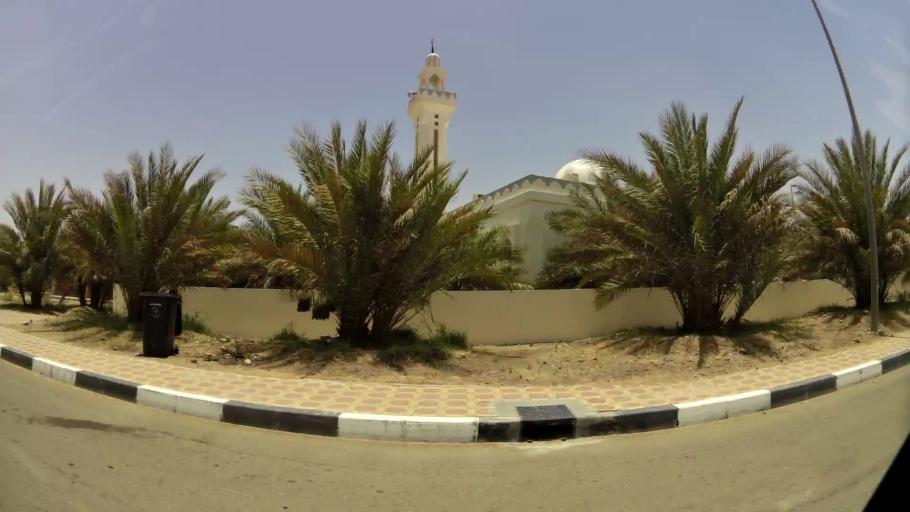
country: OM
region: Al Buraimi
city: Al Buraymi
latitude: 24.2882
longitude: 55.7359
